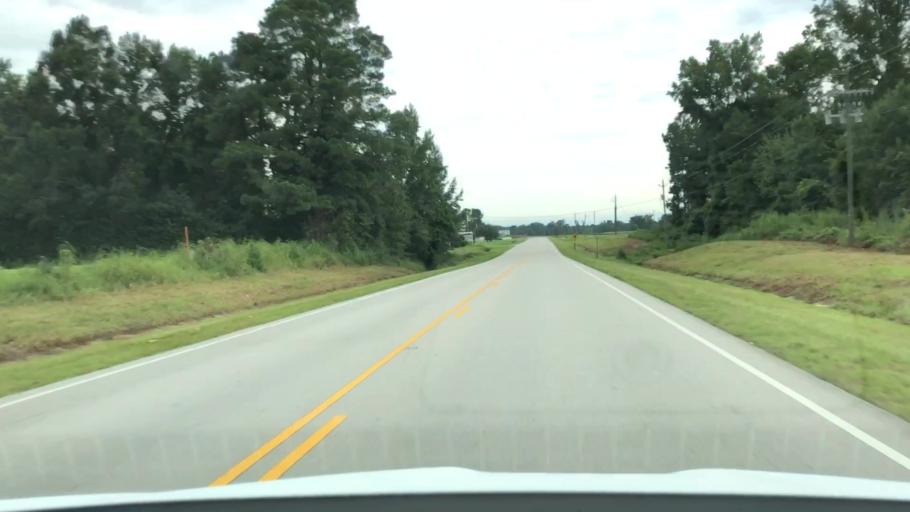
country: US
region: North Carolina
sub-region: Jones County
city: Trenton
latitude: 35.0422
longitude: -77.3504
